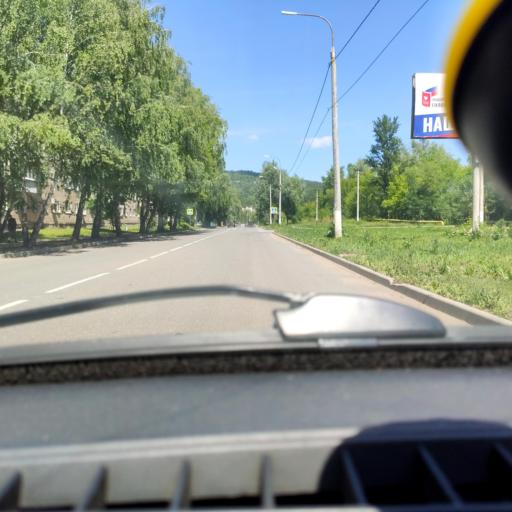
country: RU
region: Samara
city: Zhigulevsk
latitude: 53.4009
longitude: 49.5106
